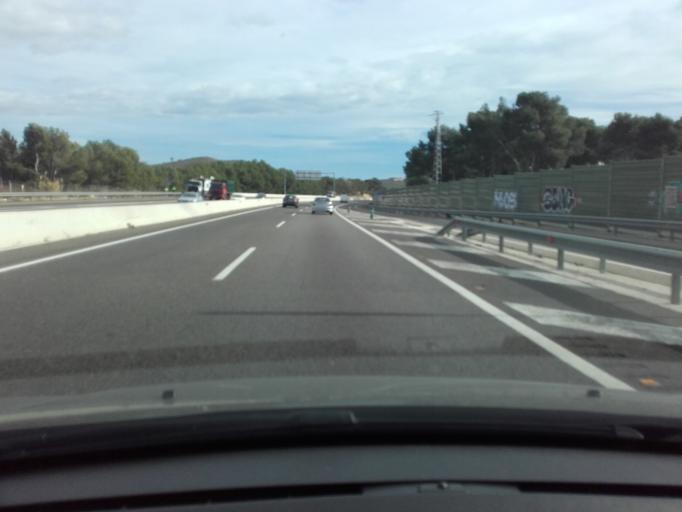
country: ES
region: Catalonia
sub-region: Provincia de Tarragona
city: el Catllar
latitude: 41.1449
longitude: 1.3173
